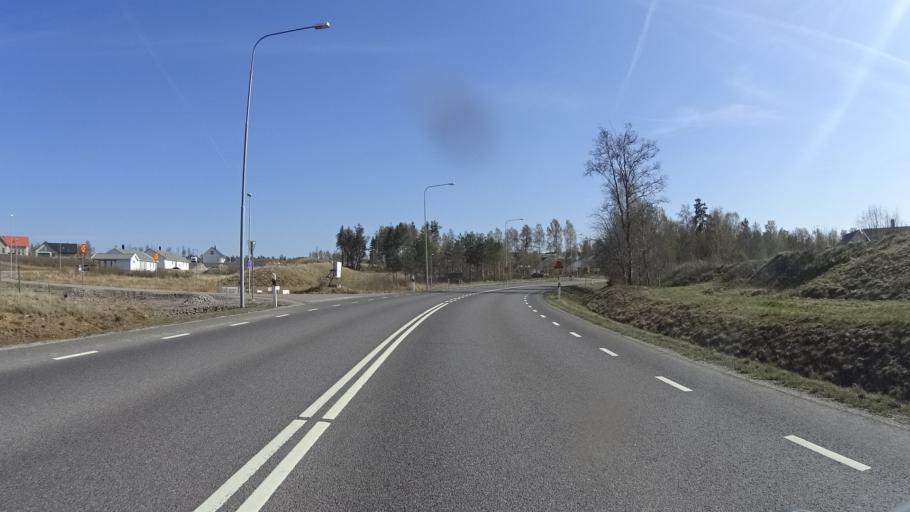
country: SE
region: Kronoberg
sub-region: Ljungby Kommun
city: Ljungby
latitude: 56.8415
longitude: 13.9741
